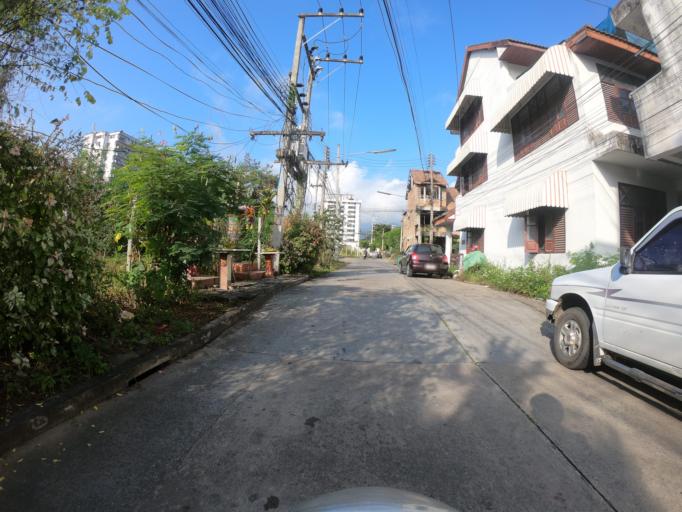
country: TH
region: Chiang Mai
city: Chiang Mai
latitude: 18.8110
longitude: 98.9646
